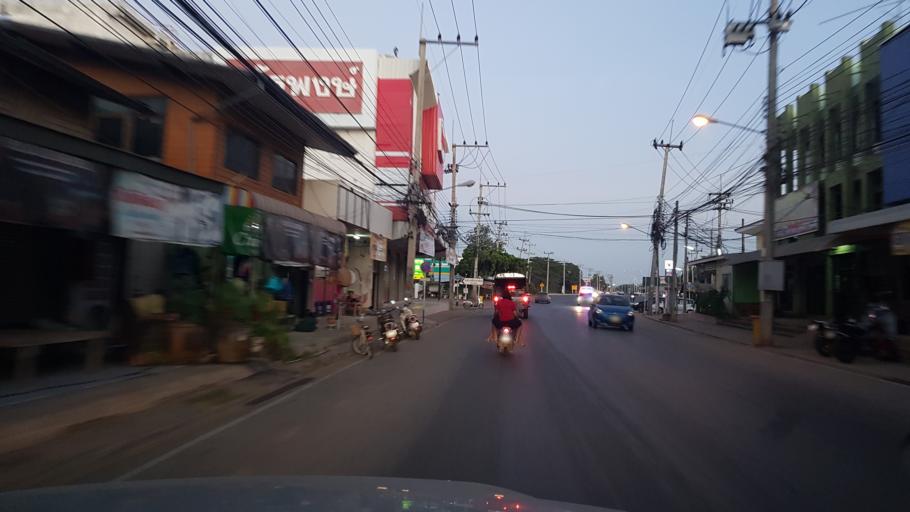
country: TH
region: Chaiyaphum
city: Phu Khiao
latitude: 16.3656
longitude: 102.1380
